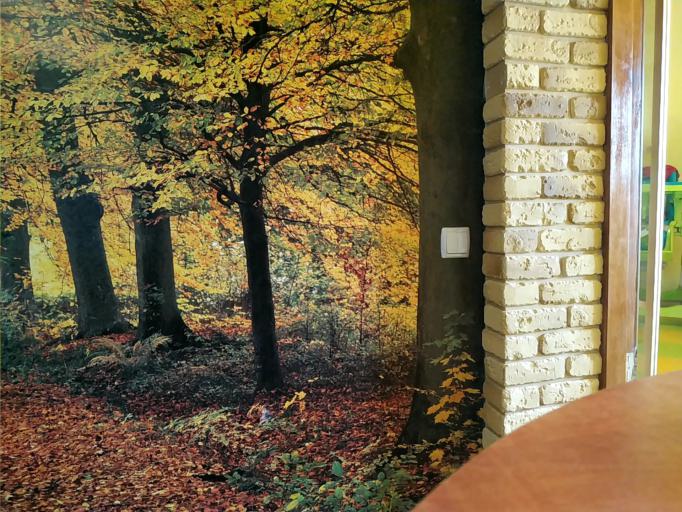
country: RU
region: Vologda
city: Nelazskoye
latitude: 59.4162
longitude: 37.6084
